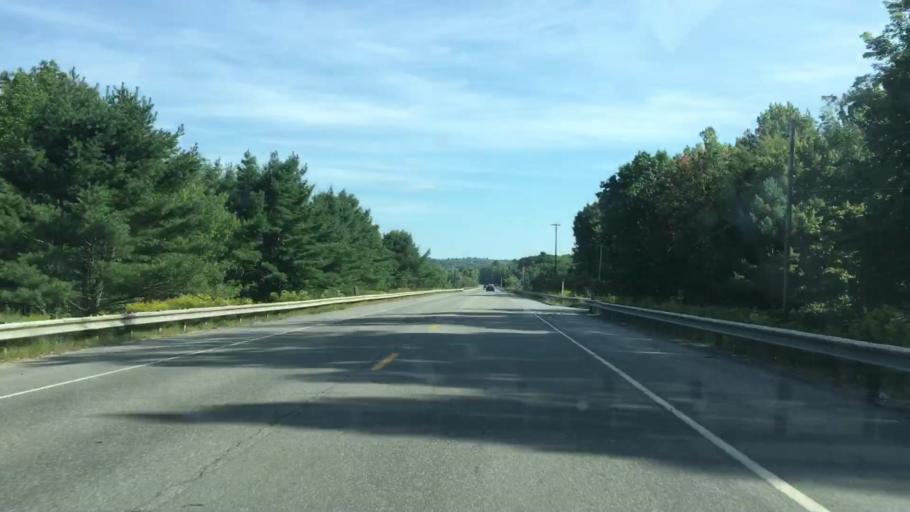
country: US
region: Maine
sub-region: Penobscot County
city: Lincoln
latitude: 45.3653
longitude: -68.5508
